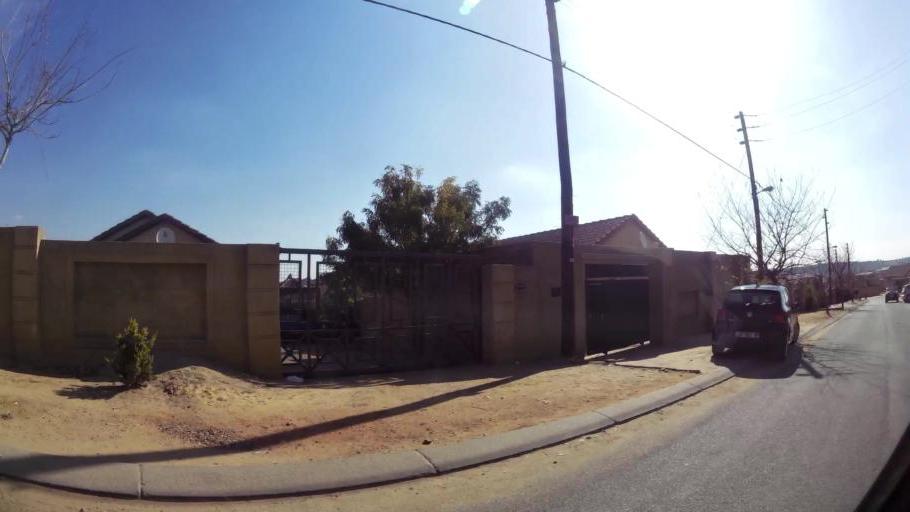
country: ZA
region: Gauteng
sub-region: West Rand District Municipality
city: Muldersdriseloop
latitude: -26.0354
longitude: 27.9224
